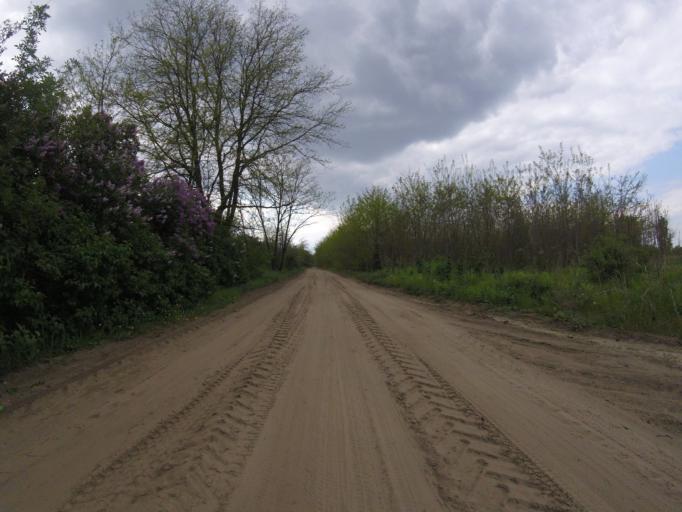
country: HU
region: Jasz-Nagykun-Szolnok
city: Jaszbereny
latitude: 47.4868
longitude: 19.8324
